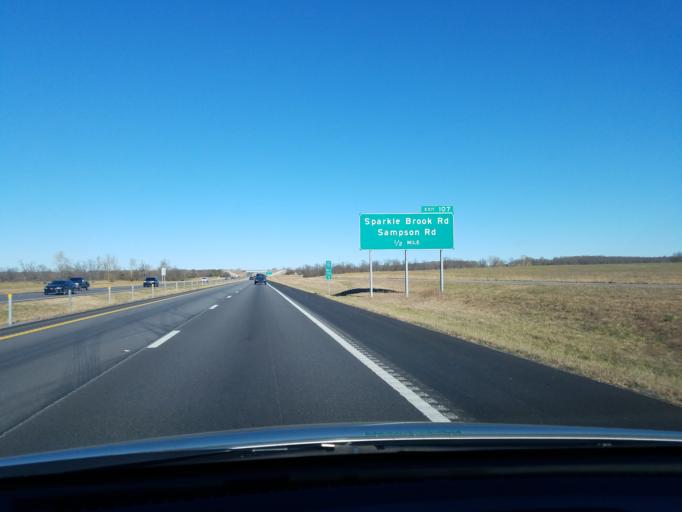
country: US
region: Missouri
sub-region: Webster County
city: Marshfield
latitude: 37.4164
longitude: -92.8864
